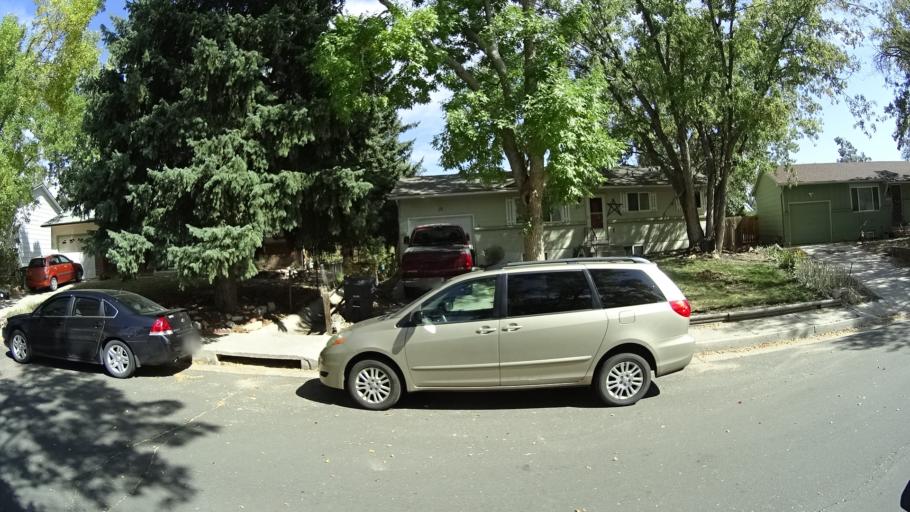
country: US
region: Colorado
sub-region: El Paso County
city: Cimarron Hills
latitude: 38.9011
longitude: -104.7553
